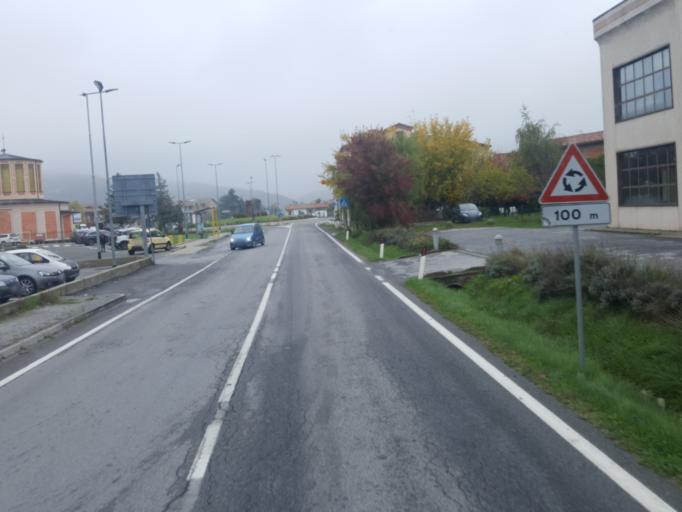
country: IT
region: Piedmont
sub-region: Provincia di Cuneo
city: Ceva
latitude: 44.3761
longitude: 8.0410
